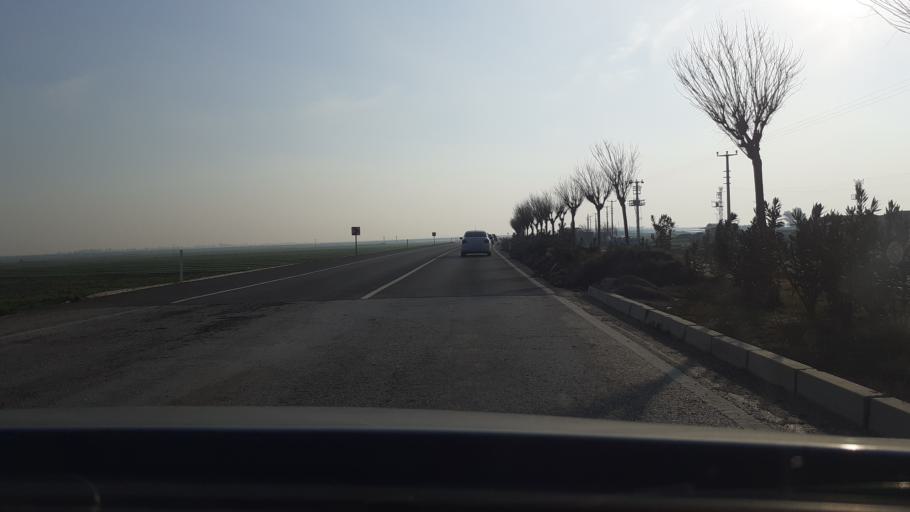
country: TR
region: Hatay
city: Serinyol
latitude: 36.3711
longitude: 36.2490
